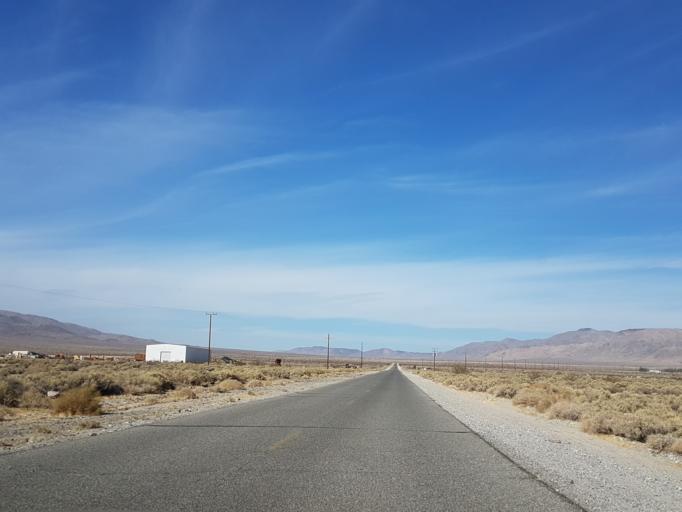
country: US
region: California
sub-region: San Bernardino County
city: Searles Valley
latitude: 35.8145
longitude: -117.3430
